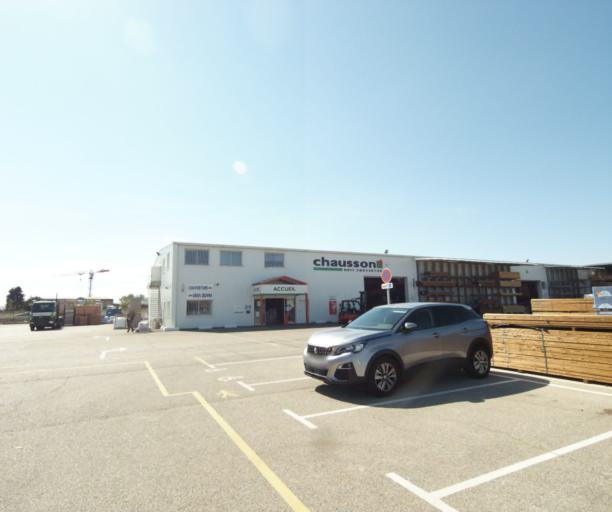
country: FR
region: Languedoc-Roussillon
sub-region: Departement du Gard
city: Bouillargues
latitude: 43.7906
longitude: 4.4333
